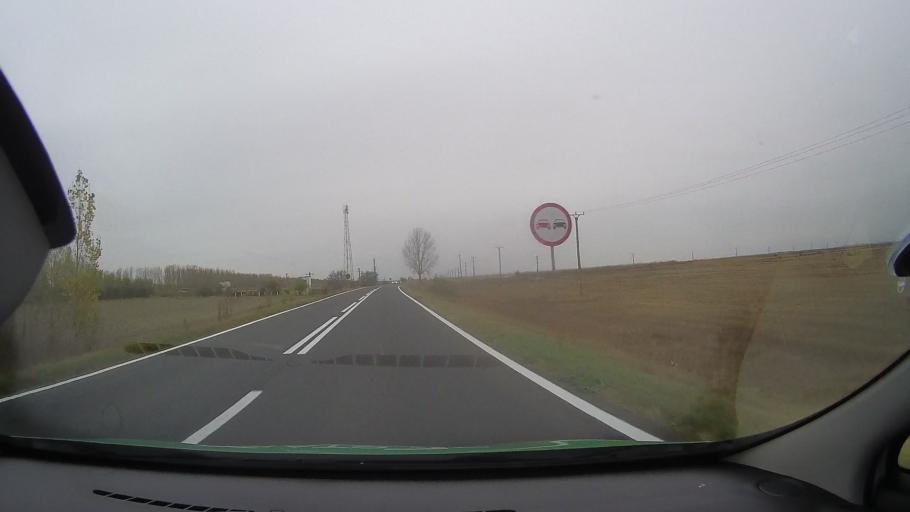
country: RO
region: Ialomita
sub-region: Comuna Giurgeni
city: Giurgeni
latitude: 44.7249
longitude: 27.8535
